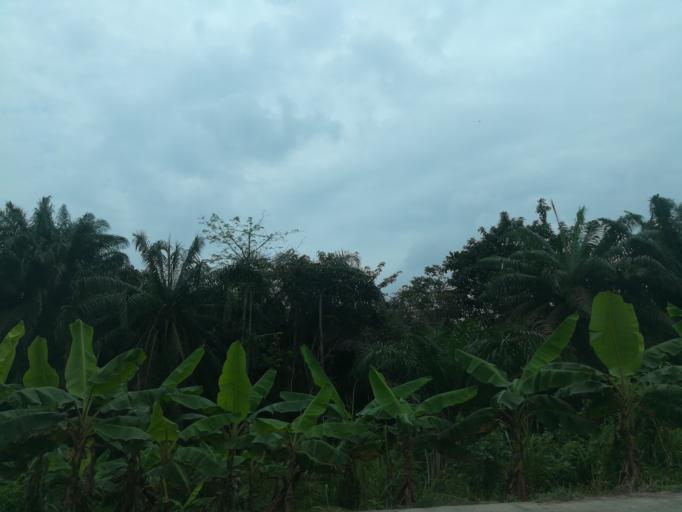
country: NG
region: Lagos
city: Ejirin
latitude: 6.6529
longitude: 3.7932
